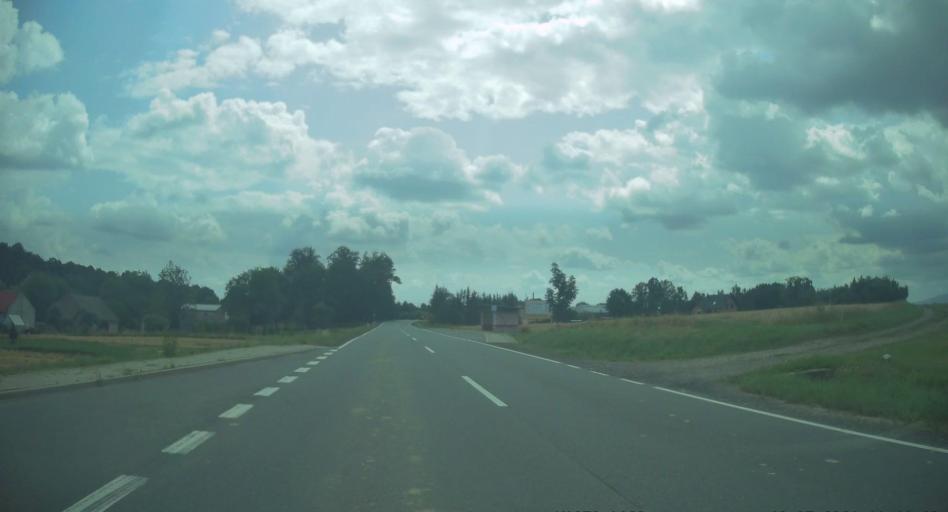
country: PL
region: Opole Voivodeship
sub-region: Powiat prudnicki
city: Laka Prudnicka
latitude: 50.3765
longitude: 17.5337
